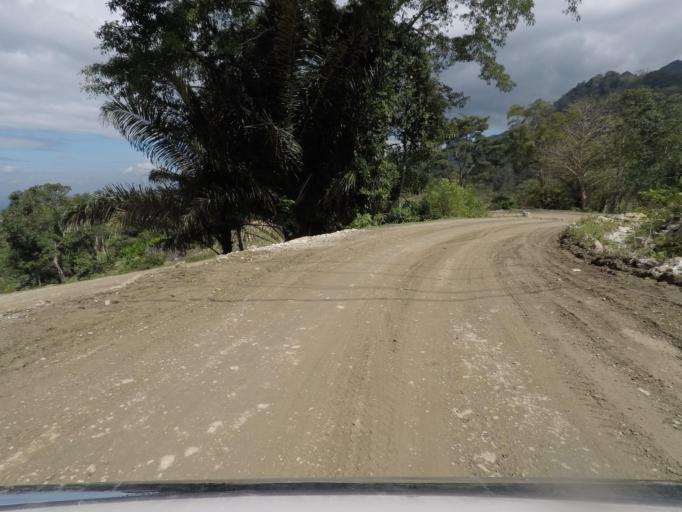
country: TL
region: Baucau
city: Venilale
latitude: -8.7341
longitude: 126.3691
